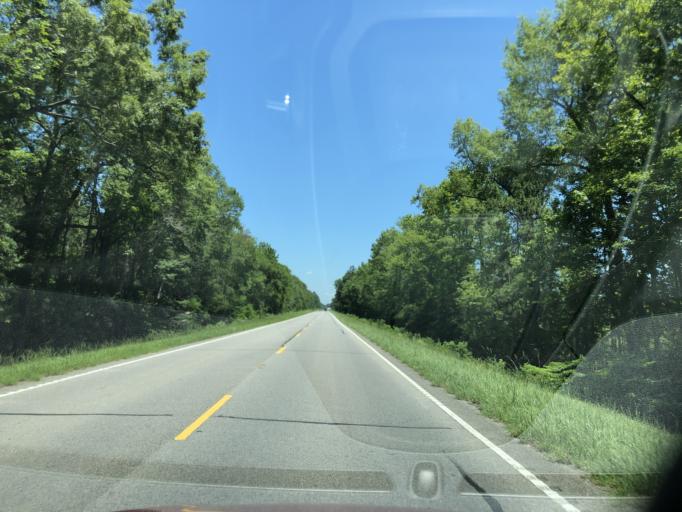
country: US
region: South Carolina
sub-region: Orangeburg County
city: Branchville
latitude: 33.2345
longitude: -80.8775
